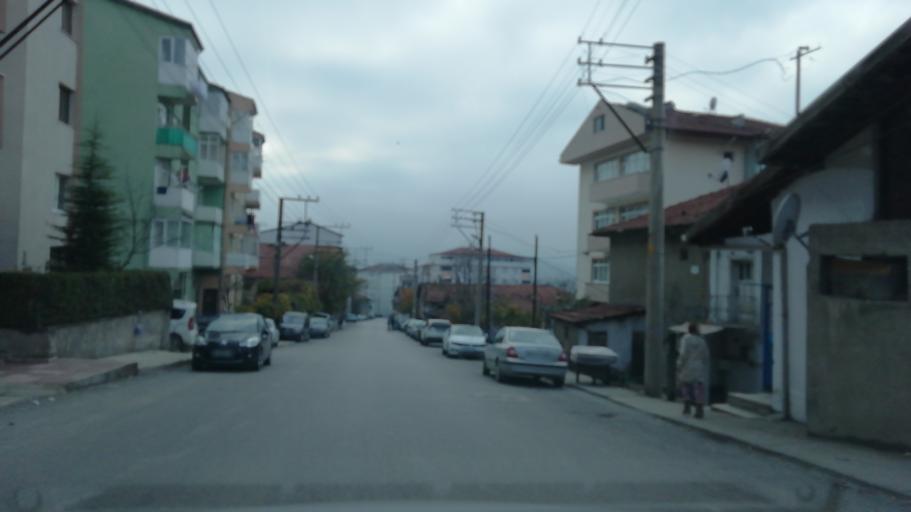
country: TR
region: Karabuk
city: Karabuk
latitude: 41.2100
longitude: 32.6277
